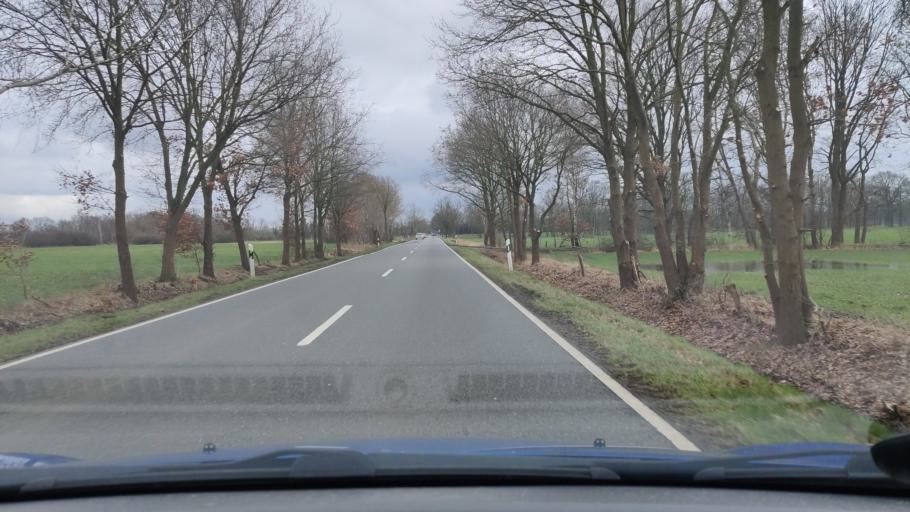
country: DE
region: Lower Saxony
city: Garbsen-Mitte
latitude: 52.4622
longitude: 9.6457
